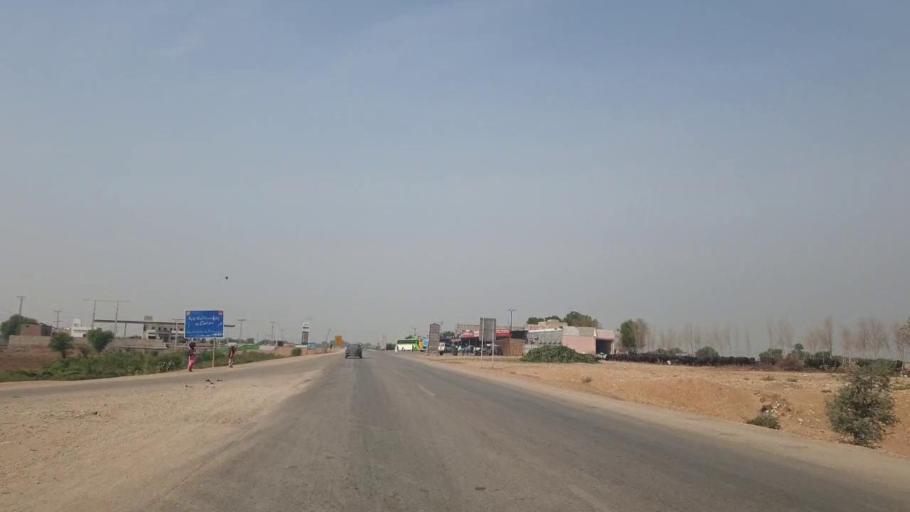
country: PK
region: Sindh
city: Sann
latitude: 26.1586
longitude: 68.0221
